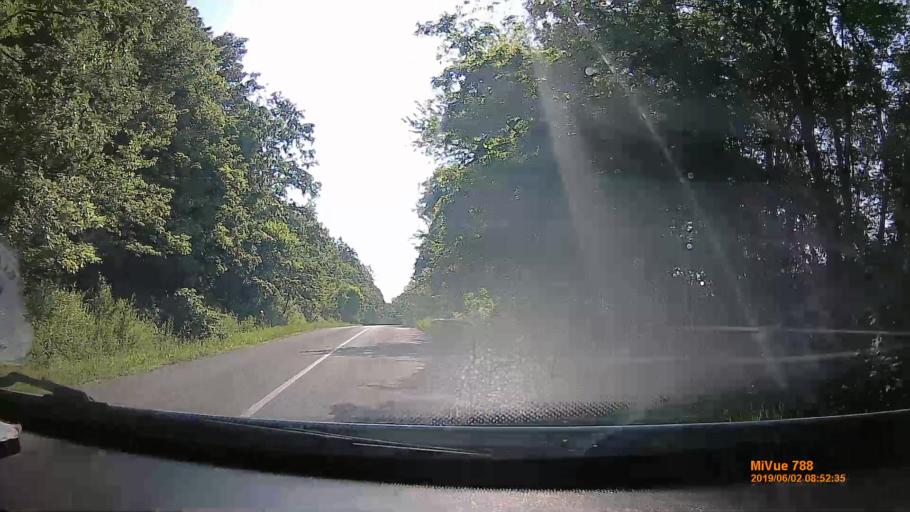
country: HU
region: Borsod-Abauj-Zemplen
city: Sajobabony
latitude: 48.1490
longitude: 20.6783
